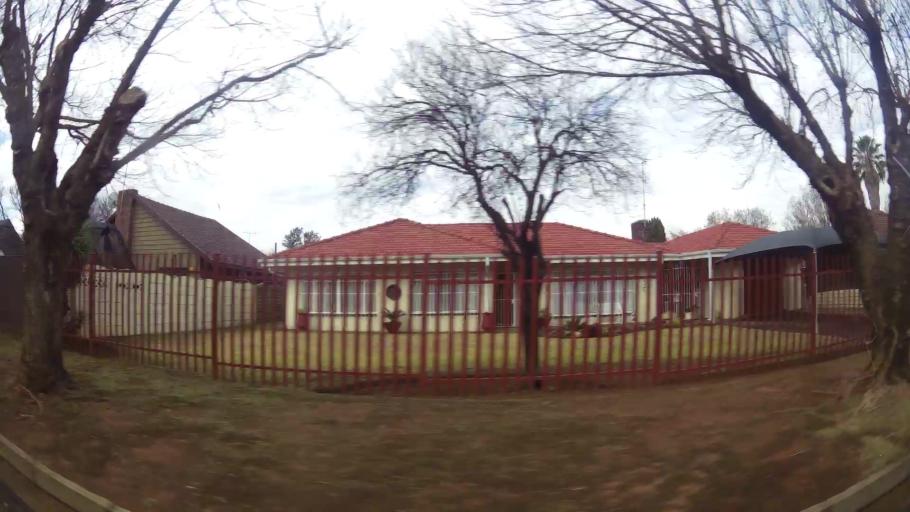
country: ZA
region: Gauteng
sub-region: Sedibeng District Municipality
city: Vereeniging
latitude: -26.6445
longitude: 27.9761
